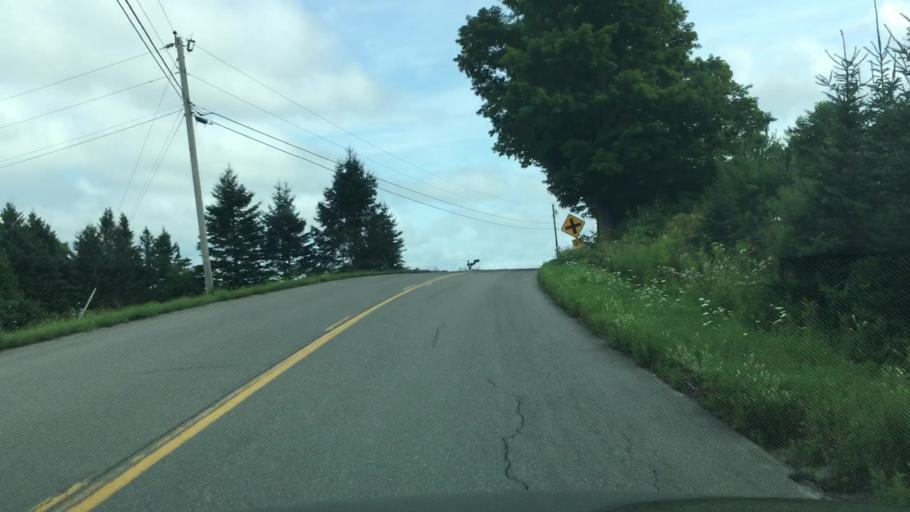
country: US
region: Maine
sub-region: Waldo County
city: Winterport
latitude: 44.6813
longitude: -68.8683
